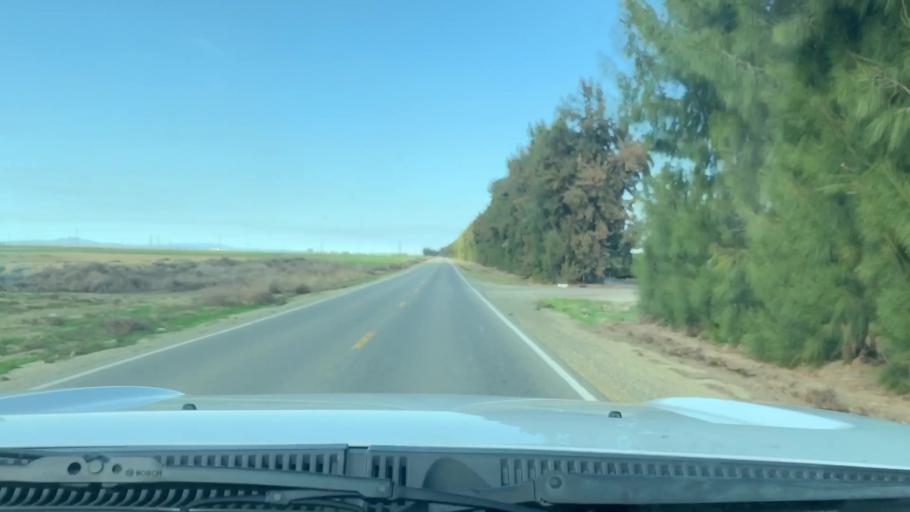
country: US
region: California
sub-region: Kern County
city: Lost Hills
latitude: 35.5203
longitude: -119.7550
